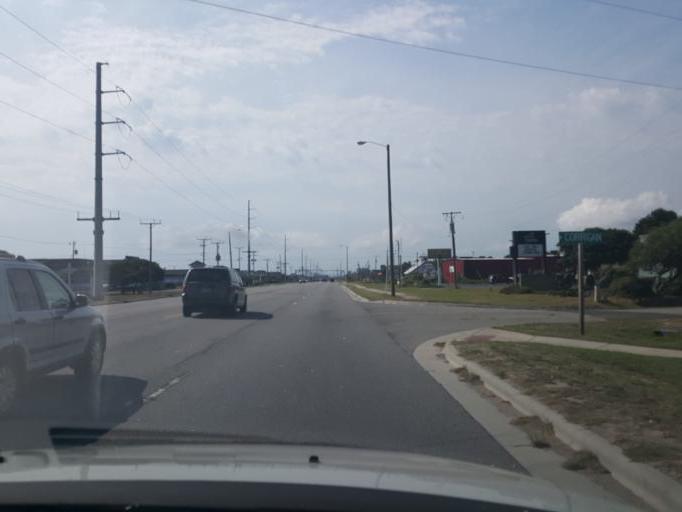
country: US
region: North Carolina
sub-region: Dare County
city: Kill Devil Hills
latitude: 36.0079
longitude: -75.6575
